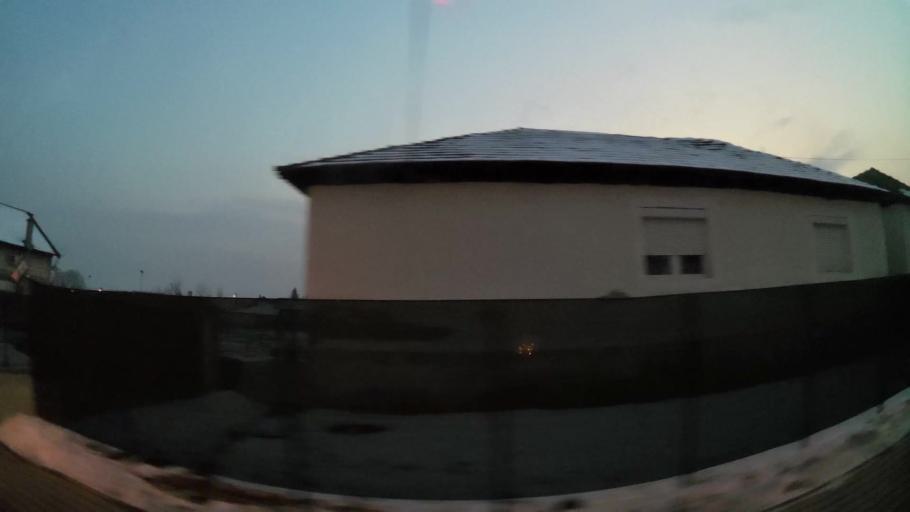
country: MK
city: Creshevo
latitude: 42.0031
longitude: 21.5187
